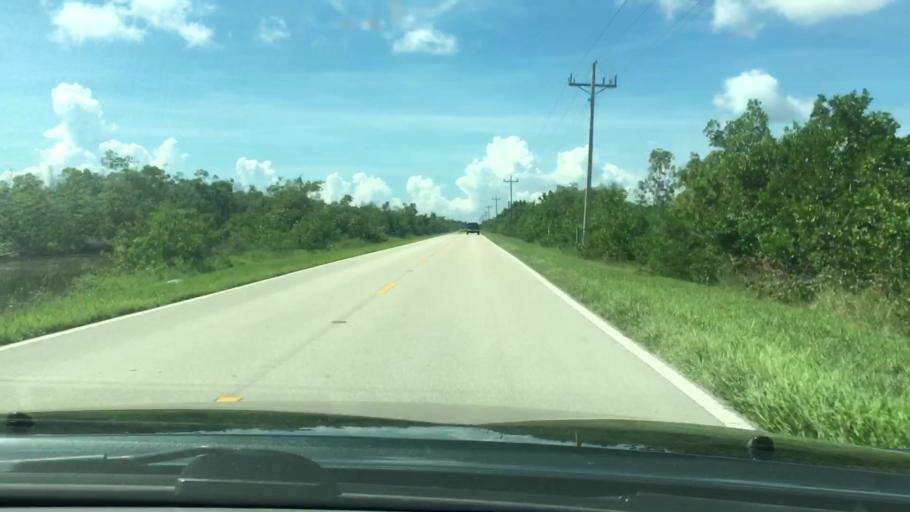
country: US
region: Florida
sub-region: Collier County
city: Marco
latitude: 25.9474
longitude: -81.6430
